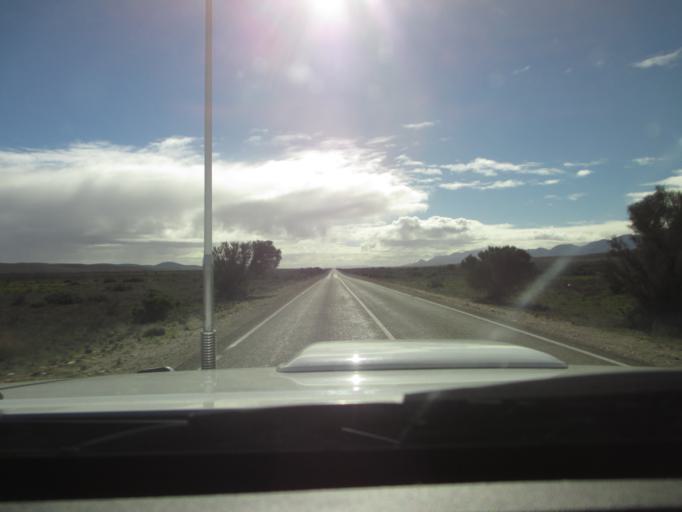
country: AU
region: South Australia
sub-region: Flinders Ranges
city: Quorn
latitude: -31.7226
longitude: 138.3468
